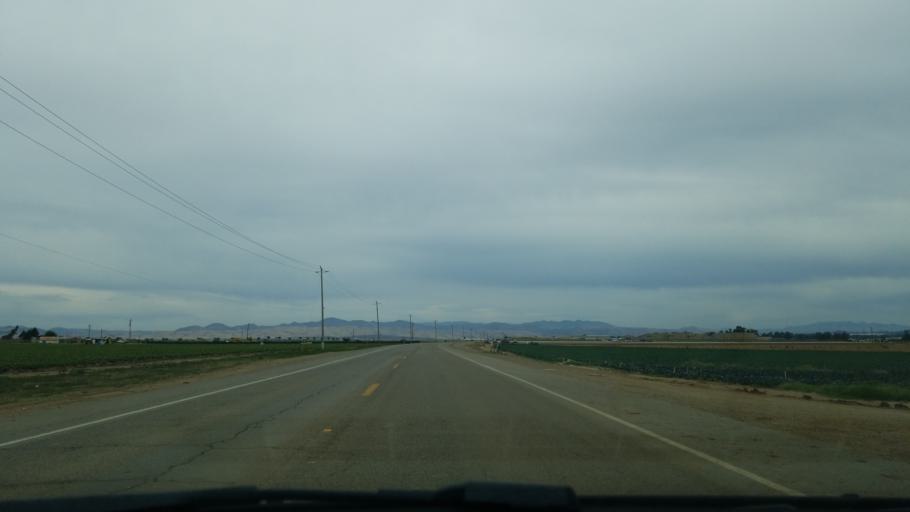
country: US
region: California
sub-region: Santa Barbara County
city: Santa Maria
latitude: 34.9200
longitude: -120.5026
